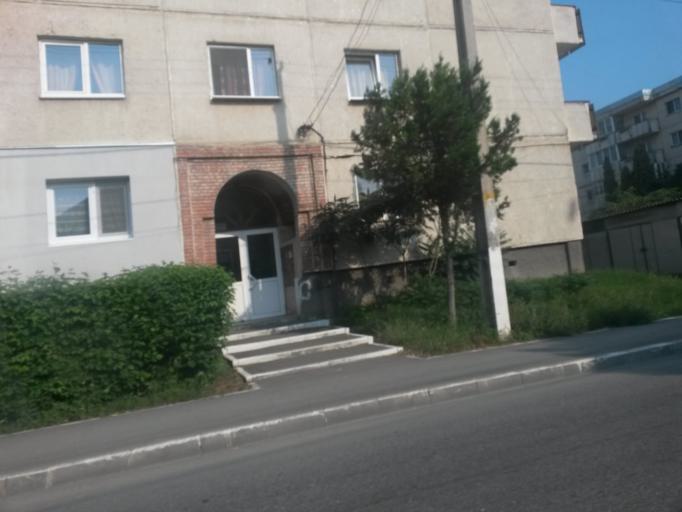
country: RO
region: Cluj
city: Turda
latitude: 46.5688
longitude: 23.7800
